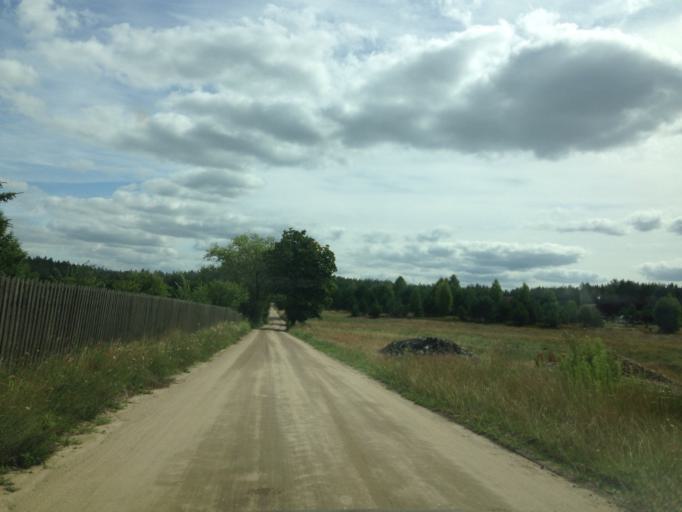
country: PL
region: Pomeranian Voivodeship
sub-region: Powiat bytowski
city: Studzienice
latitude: 54.0730
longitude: 17.6799
